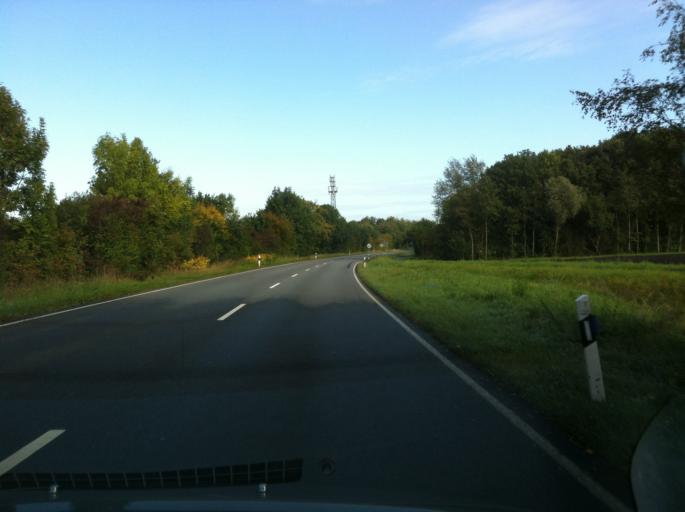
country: DE
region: North Rhine-Westphalia
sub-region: Regierungsbezirk Munster
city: Ochtrup
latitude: 52.2563
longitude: 7.1633
